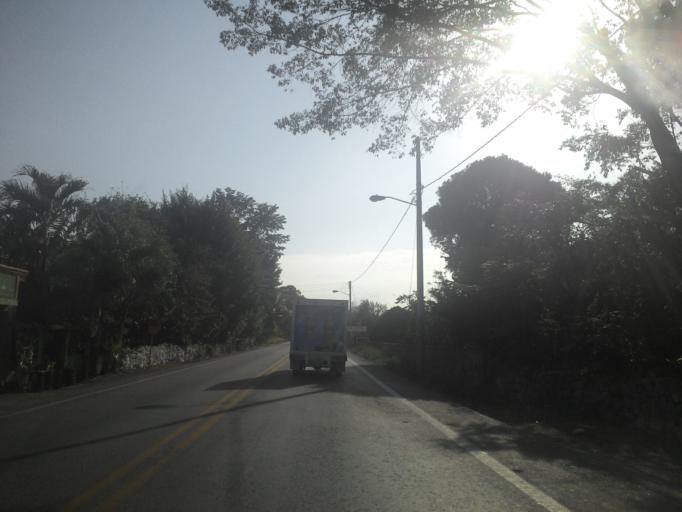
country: MX
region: Yucatan
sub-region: Valladolid
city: Tikuch
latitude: 20.7014
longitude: -88.1141
